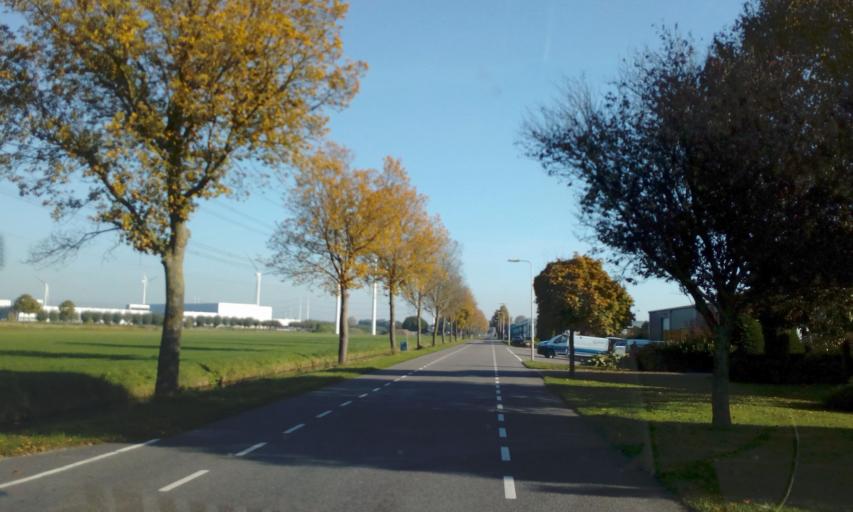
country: NL
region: South Holland
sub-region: Gemeente Zoetermeer
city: Zoetermeer
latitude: 52.0310
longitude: 4.4908
